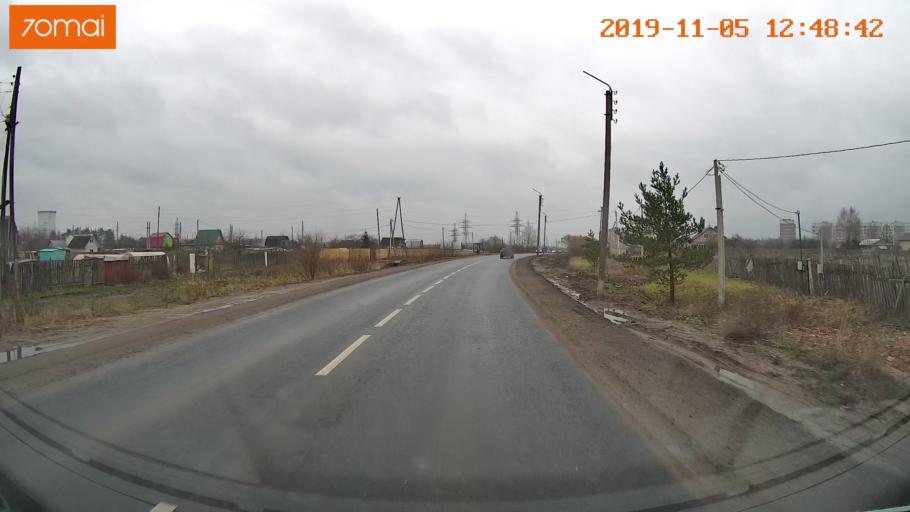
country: RU
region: Ivanovo
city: Kokhma
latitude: 56.9591
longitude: 41.1001
